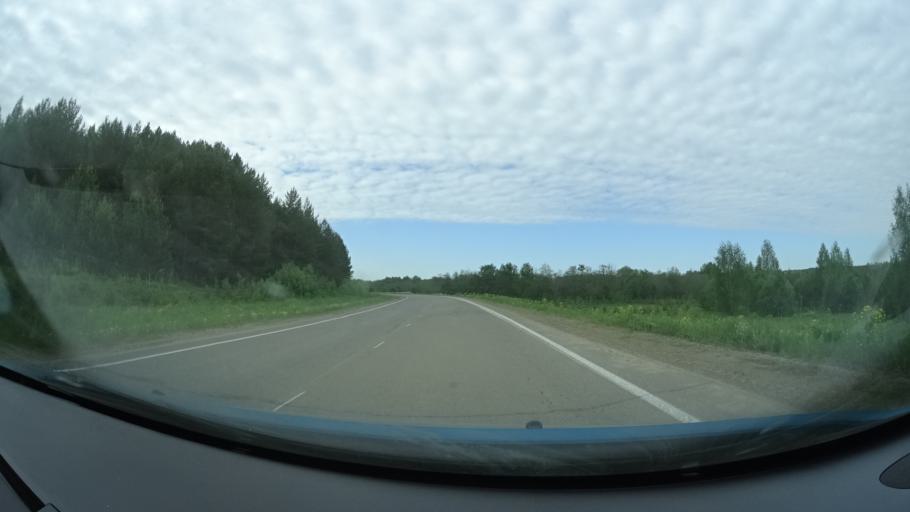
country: RU
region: Perm
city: Kuyeda
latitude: 56.5226
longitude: 55.6264
